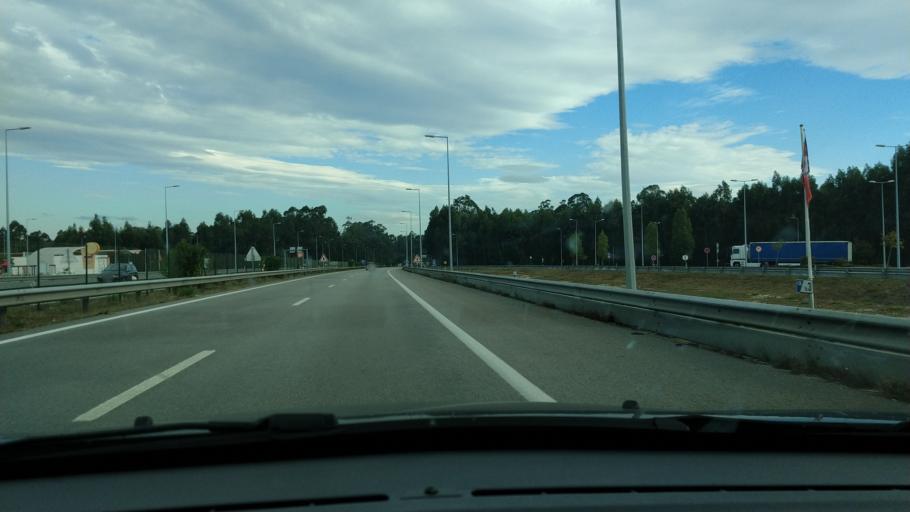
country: PT
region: Aveiro
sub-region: Aveiro
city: Eixo
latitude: 40.6603
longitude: -8.5919
